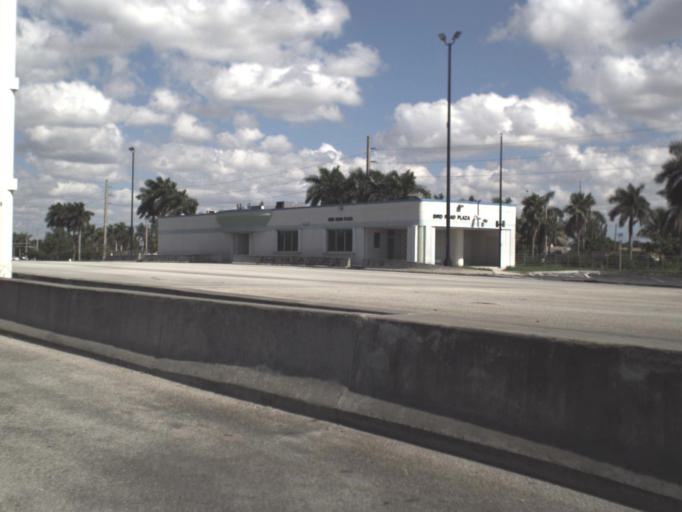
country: US
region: Florida
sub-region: Miami-Dade County
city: Westwood Lake
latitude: 25.7195
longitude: -80.3838
